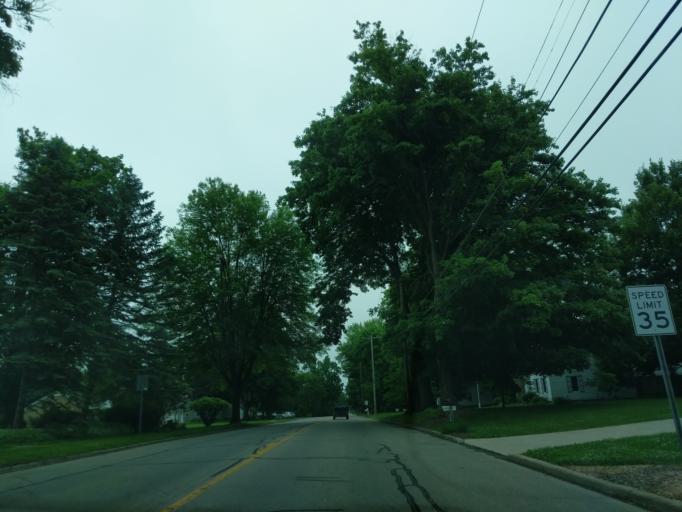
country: US
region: Michigan
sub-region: Hillsdale County
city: Litchfield
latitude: 42.0481
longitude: -84.7638
